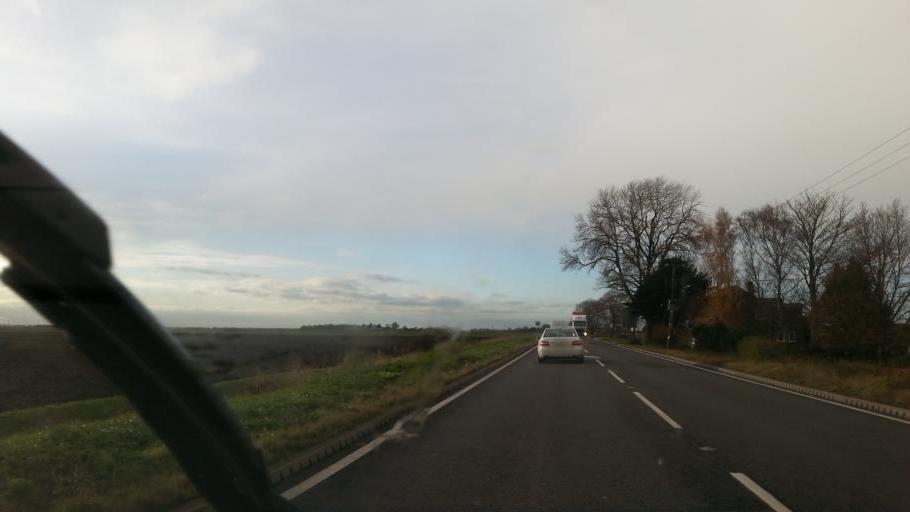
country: GB
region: England
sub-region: Peterborough
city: Thorney
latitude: 52.6146
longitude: -0.0014
